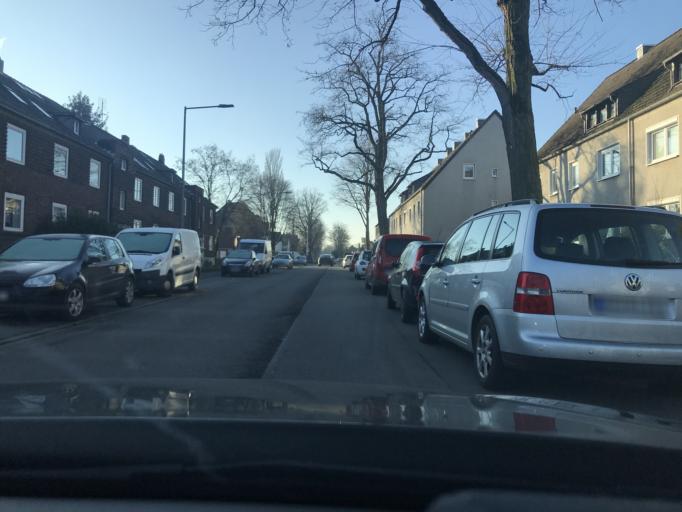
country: DE
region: North Rhine-Westphalia
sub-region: Regierungsbezirk Dusseldorf
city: Krefeld
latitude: 51.3404
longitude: 6.6173
